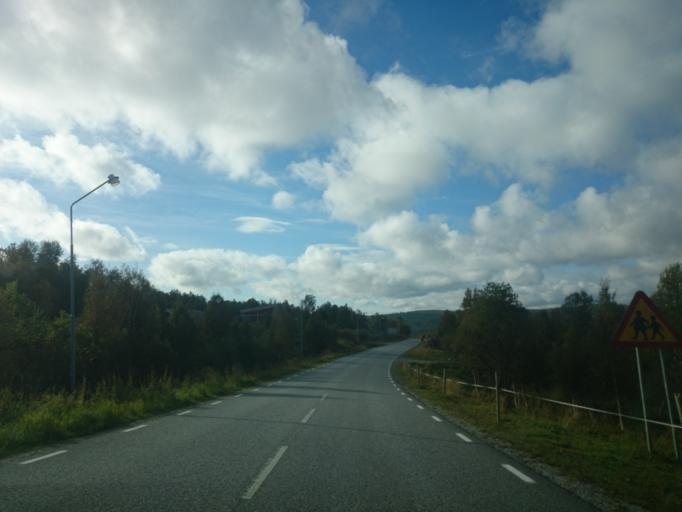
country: NO
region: Sor-Trondelag
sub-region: Tydal
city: Aas
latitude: 62.6360
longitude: 12.4450
